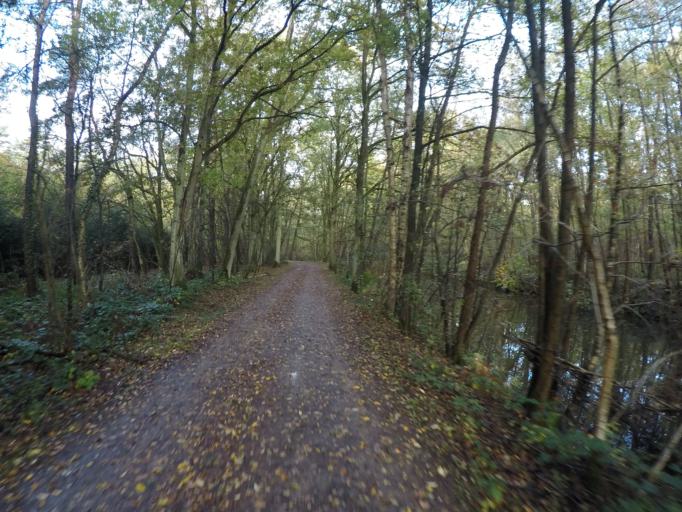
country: BE
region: Flanders
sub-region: Provincie Antwerpen
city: Schilde
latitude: 51.2382
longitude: 4.6069
